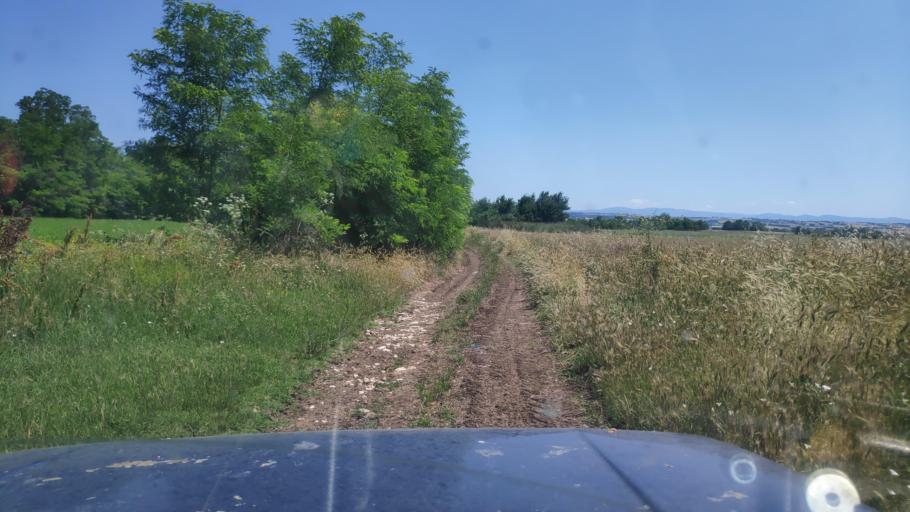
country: MK
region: Kumanovo
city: Bedinje
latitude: 42.1687
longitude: 21.6861
